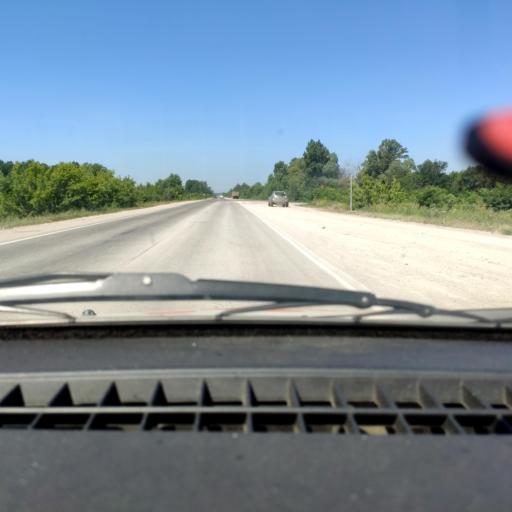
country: RU
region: Bashkortostan
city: Sterlitamak
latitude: 53.6401
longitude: 56.0630
